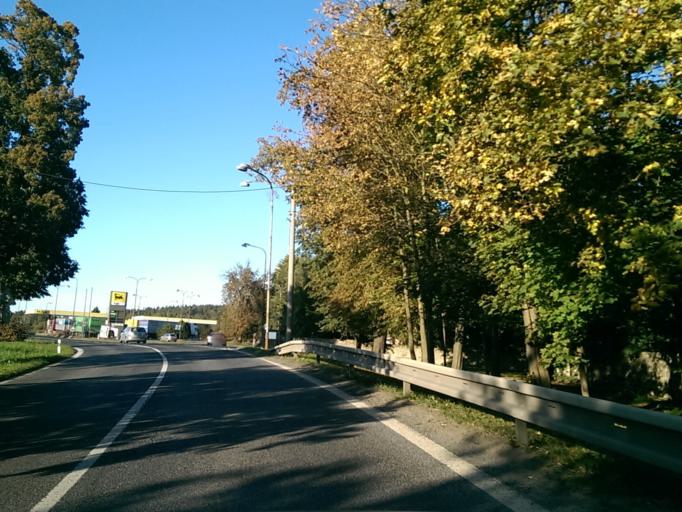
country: CZ
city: Duba
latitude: 50.5490
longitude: 14.5437
